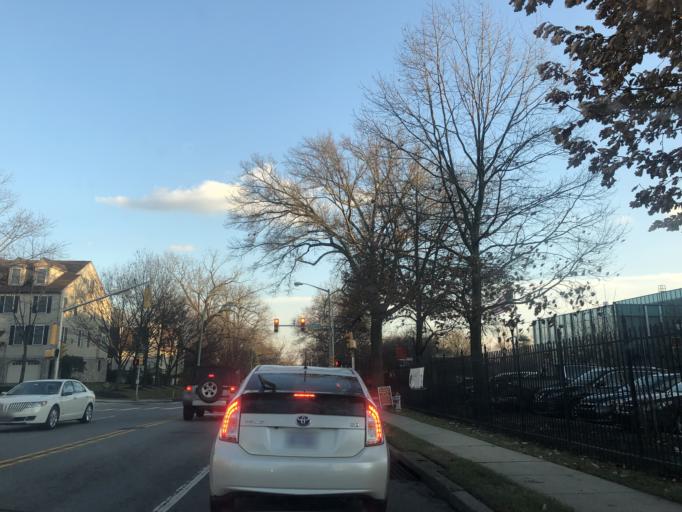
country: US
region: Pennsylvania
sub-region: Montgomery County
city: Bryn Mawr
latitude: 40.0151
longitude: -75.3053
